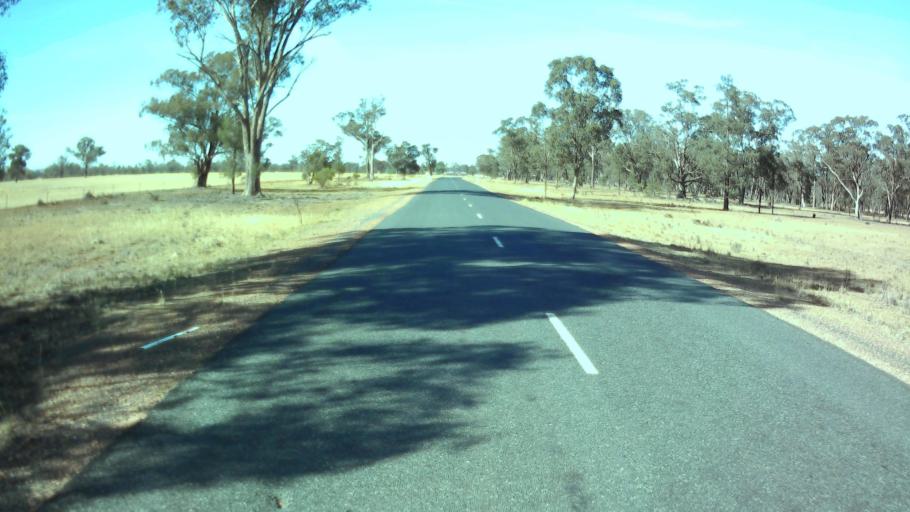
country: AU
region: New South Wales
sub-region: Weddin
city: Grenfell
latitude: -34.0930
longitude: 147.8875
